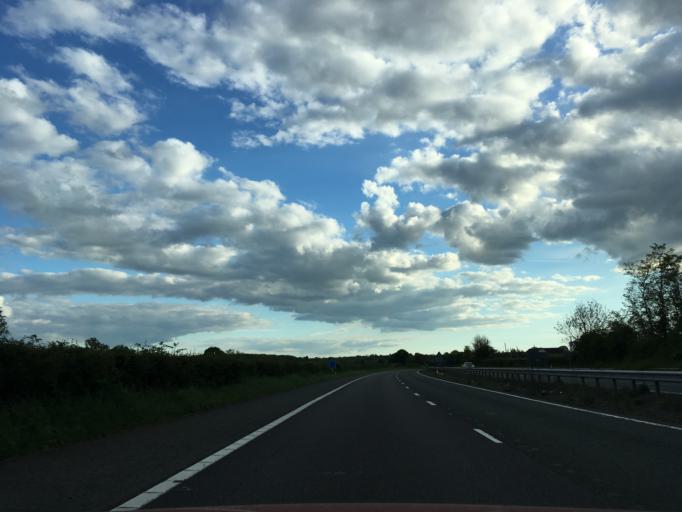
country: GB
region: England
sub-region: Herefordshire
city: Donnington
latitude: 51.9854
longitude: -2.4020
